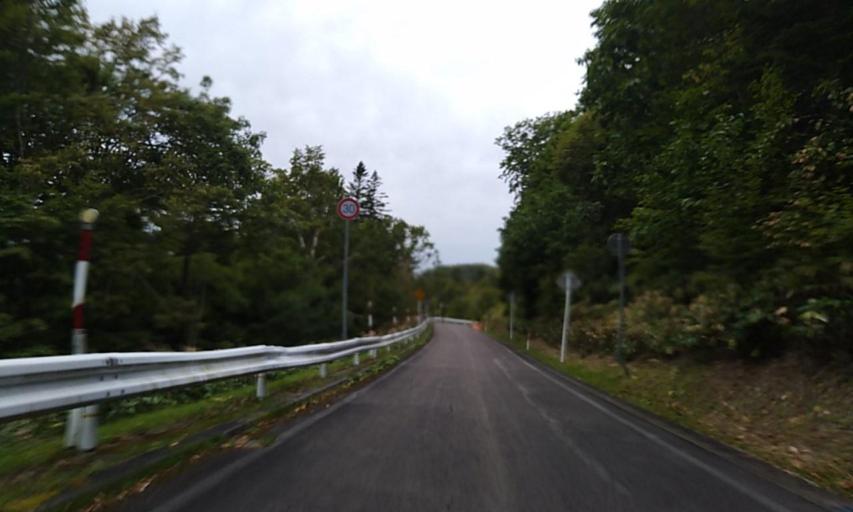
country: JP
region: Hokkaido
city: Bihoro
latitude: 43.5689
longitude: 144.2029
